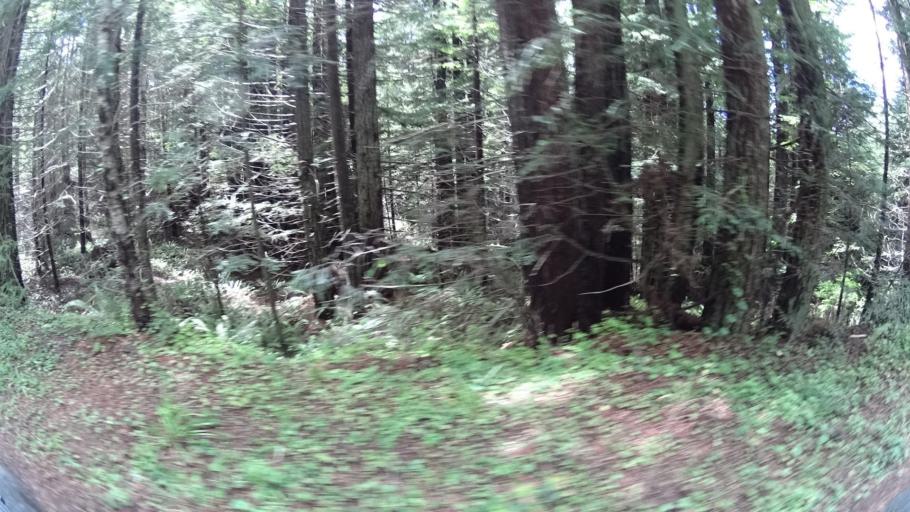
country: US
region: California
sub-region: Humboldt County
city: Blue Lake
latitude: 40.8464
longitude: -123.9246
